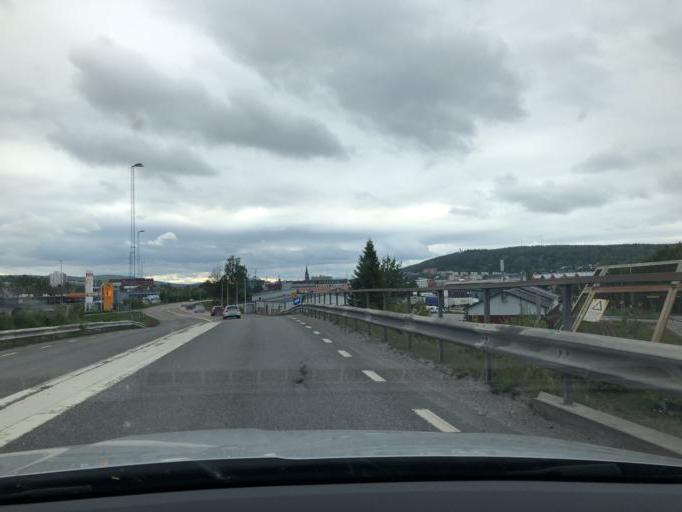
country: SE
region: Vaesternorrland
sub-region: Sundsvalls Kommun
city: Sundsvall
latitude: 62.3853
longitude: 17.3297
